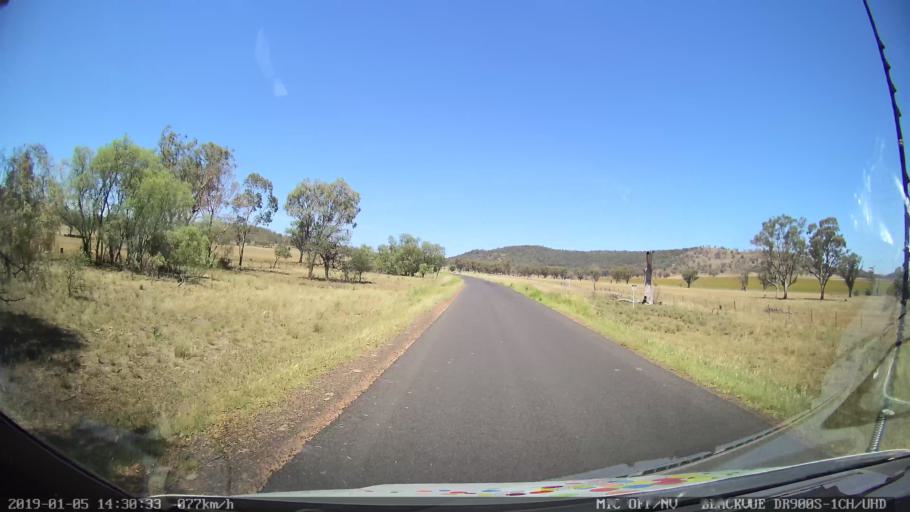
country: AU
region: New South Wales
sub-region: Tamworth Municipality
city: Phillip
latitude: -31.2278
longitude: 150.5944
